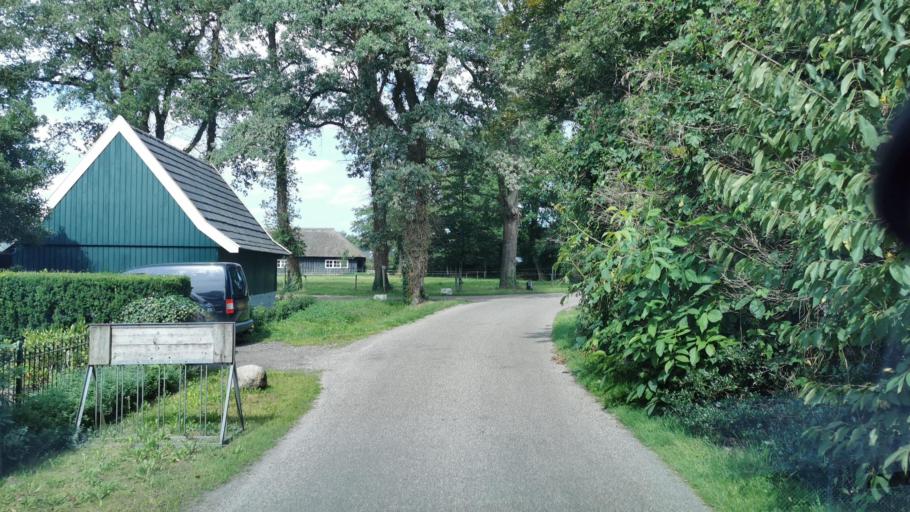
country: NL
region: Overijssel
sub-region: Gemeente Enschede
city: Enschede
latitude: 52.1791
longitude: 6.8663
